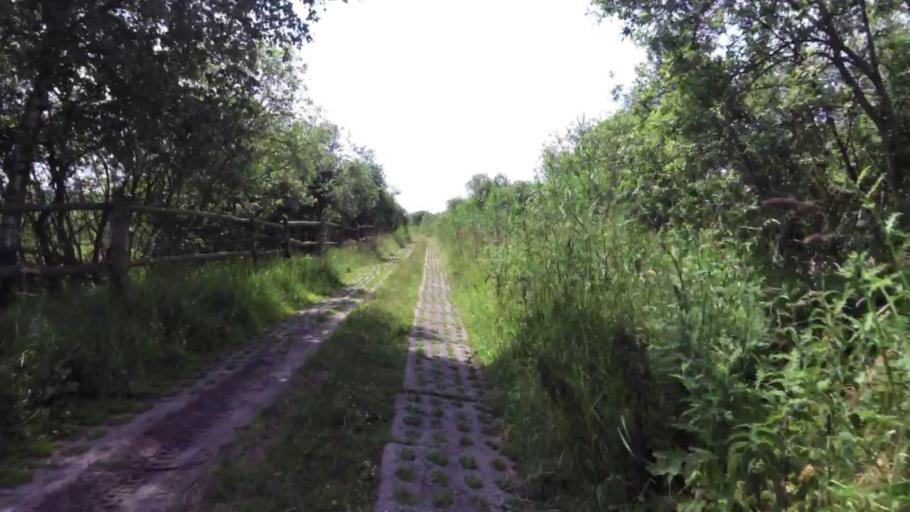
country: PL
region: West Pomeranian Voivodeship
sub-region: Powiat goleniowski
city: Stepnica
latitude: 53.7149
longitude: 14.5906
